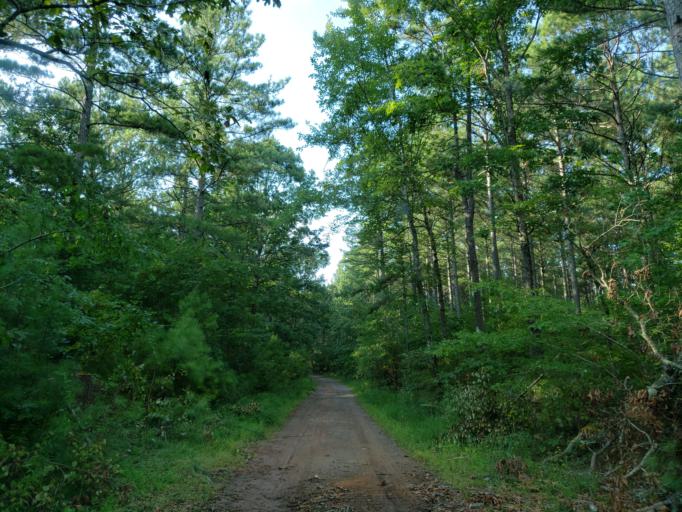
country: US
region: Georgia
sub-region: Cobb County
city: Acworth
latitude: 34.1765
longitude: -84.6447
